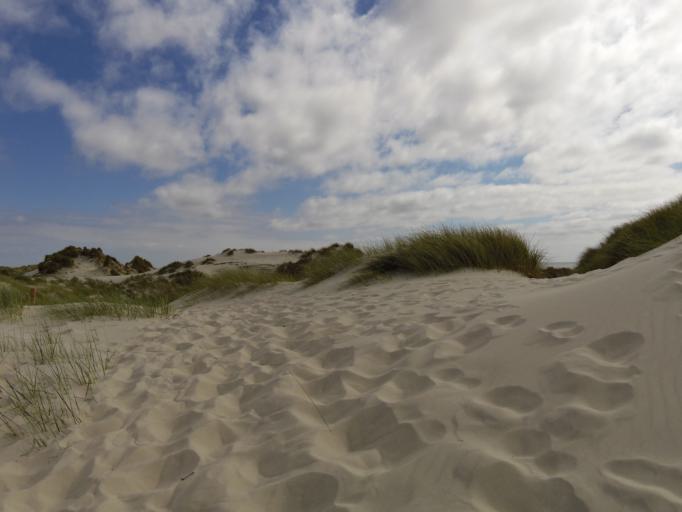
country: DE
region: Schleswig-Holstein
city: Wittdun
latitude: 54.6227
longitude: 8.3615
